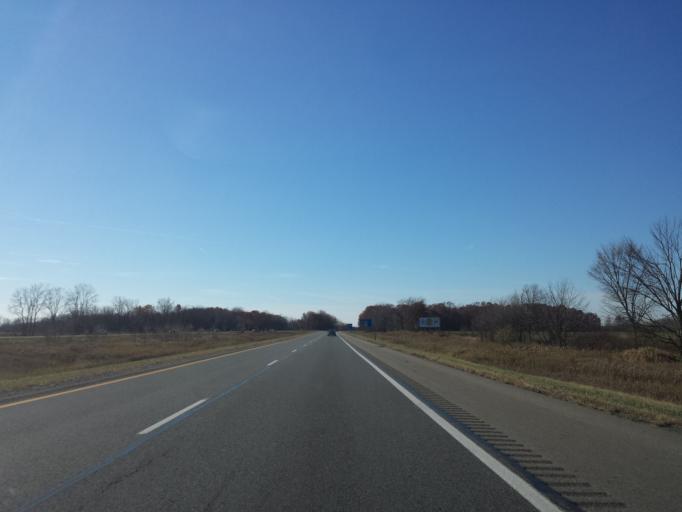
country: US
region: Michigan
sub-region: Ingham County
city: Williamston
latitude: 42.6659
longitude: -84.2628
